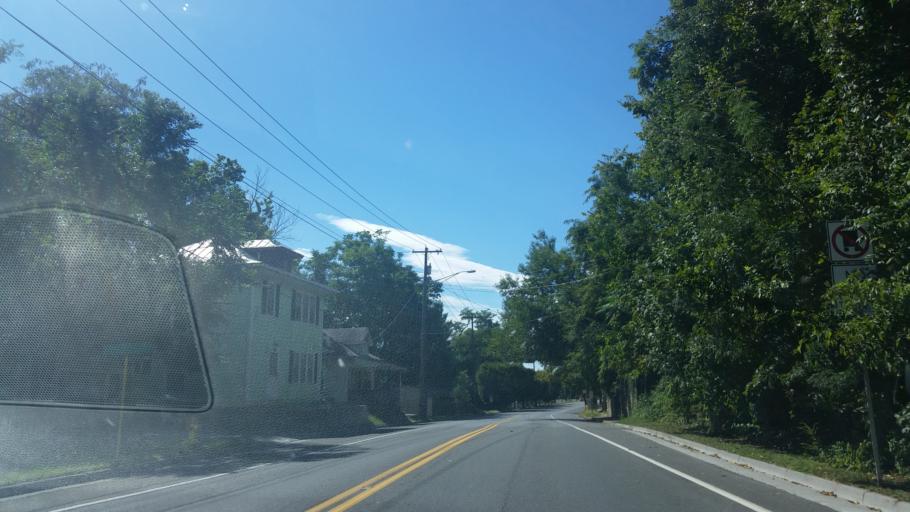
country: US
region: Virginia
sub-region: City of Winchester
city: Winchester
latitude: 39.1992
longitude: -78.1643
